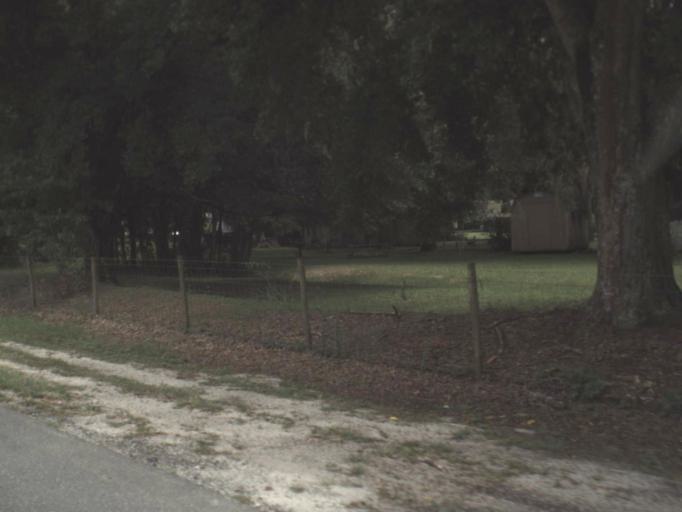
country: US
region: Florida
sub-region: Pasco County
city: Lacoochee
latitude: 28.4682
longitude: -82.1655
